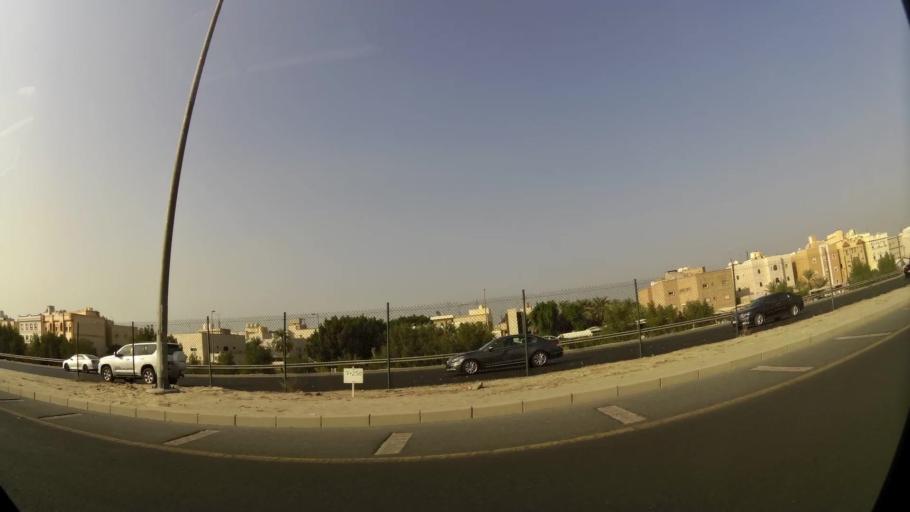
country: KW
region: Al Asimah
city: Ar Rabiyah
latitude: 29.2969
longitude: 47.8837
